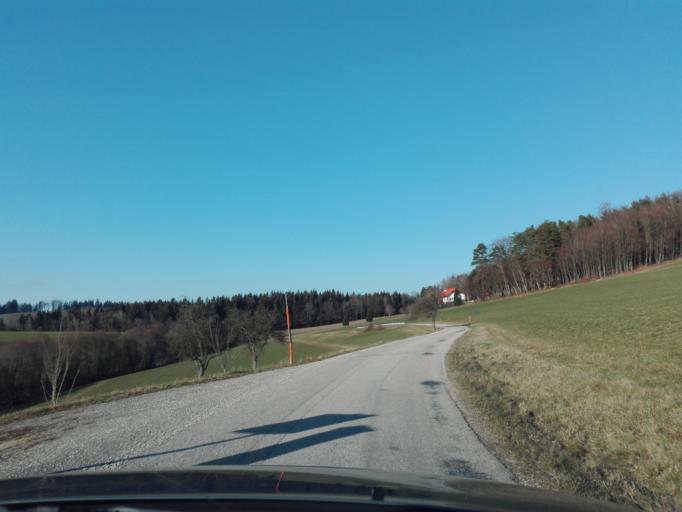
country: AT
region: Upper Austria
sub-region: Politischer Bezirk Rohrbach
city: Kleinzell im Muehlkreis
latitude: 48.3895
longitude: 13.9510
